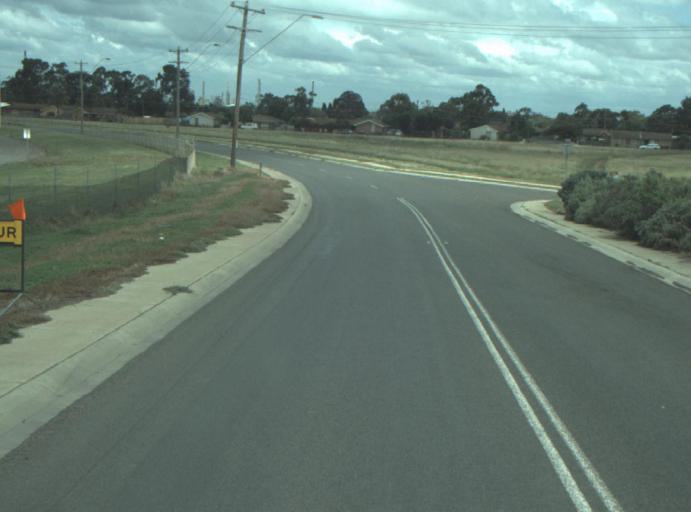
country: AU
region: Victoria
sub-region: Greater Geelong
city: Lara
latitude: -38.0609
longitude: 144.3780
